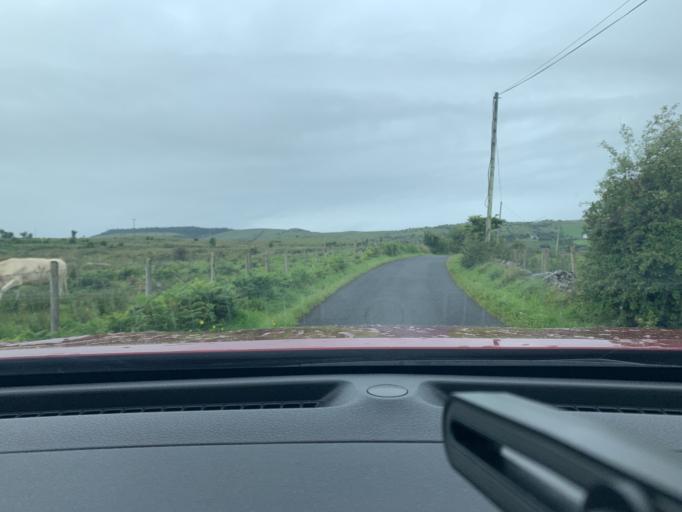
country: GB
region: Northern Ireland
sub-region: Fermanagh District
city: Enniskillen
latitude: 54.2586
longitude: -7.8476
